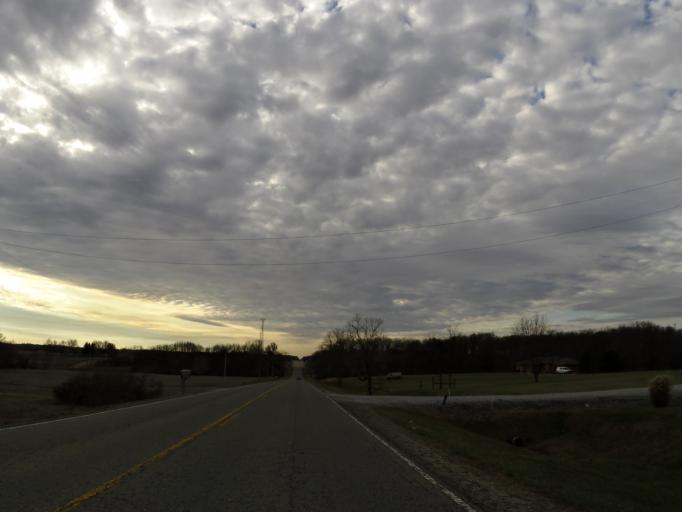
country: US
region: Illinois
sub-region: Jefferson County
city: Mount Vernon
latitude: 38.3713
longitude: -89.0347
